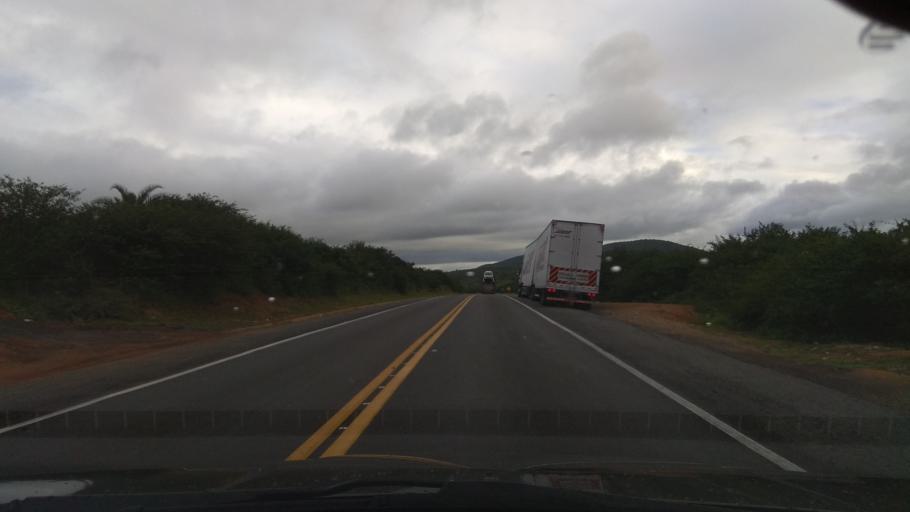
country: BR
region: Bahia
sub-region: Santa Ines
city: Santa Ines
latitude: -13.2859
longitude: -40.0203
